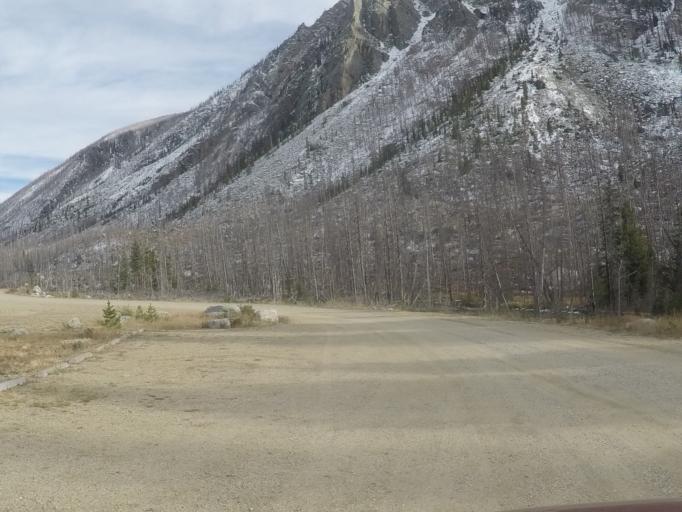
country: US
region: Montana
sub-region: Carbon County
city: Red Lodge
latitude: 45.1684
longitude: -109.4959
